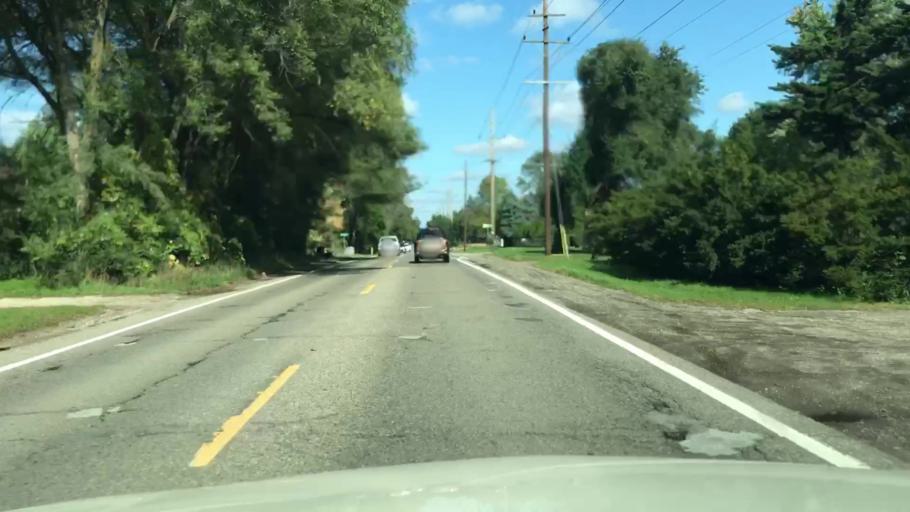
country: US
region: Michigan
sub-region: Oakland County
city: Rochester
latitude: 42.6429
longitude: -83.0923
